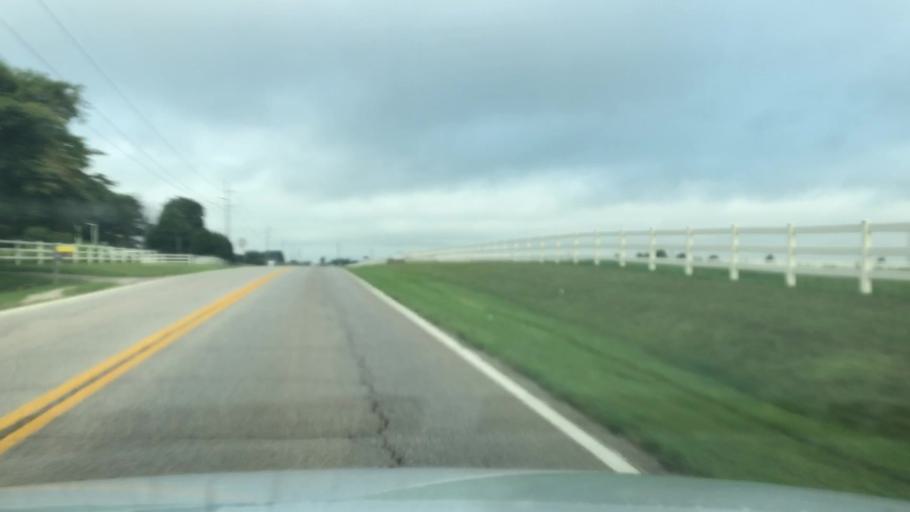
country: US
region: Oklahoma
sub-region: Nowata County
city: Nowata
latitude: 36.7136
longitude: -95.6867
